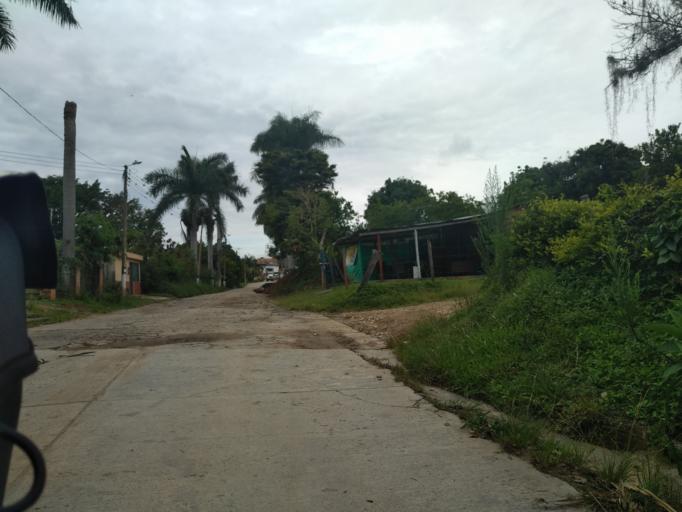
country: CO
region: Santander
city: Guepsa
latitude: 6.0263
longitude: -73.5700
